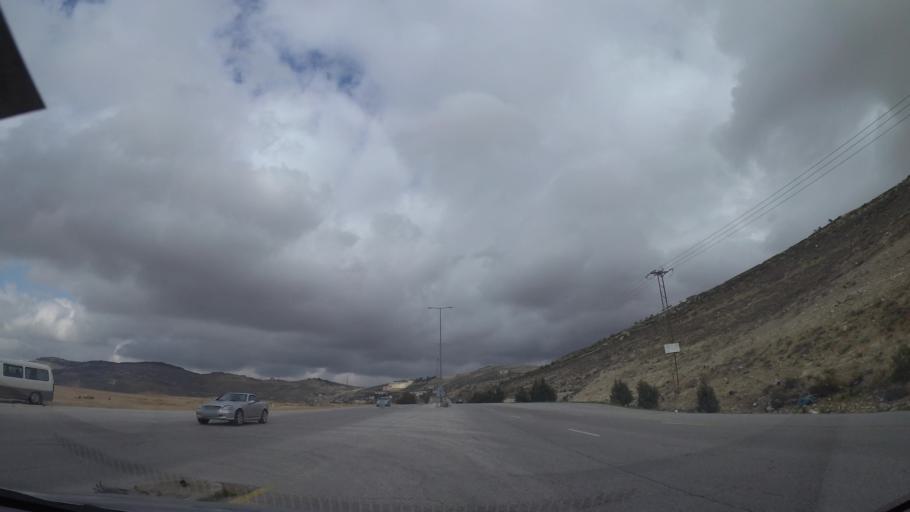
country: JO
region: Amman
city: Al Jubayhah
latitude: 32.0842
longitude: 35.8854
